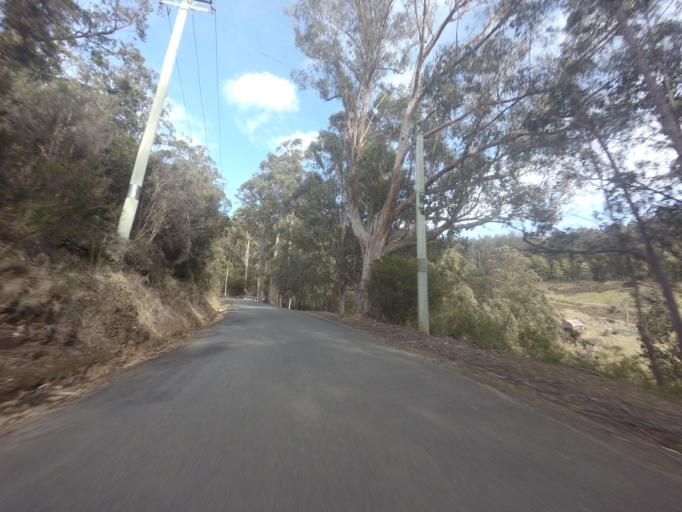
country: AU
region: Tasmania
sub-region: Kingborough
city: Margate
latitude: -43.0064
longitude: 147.1695
